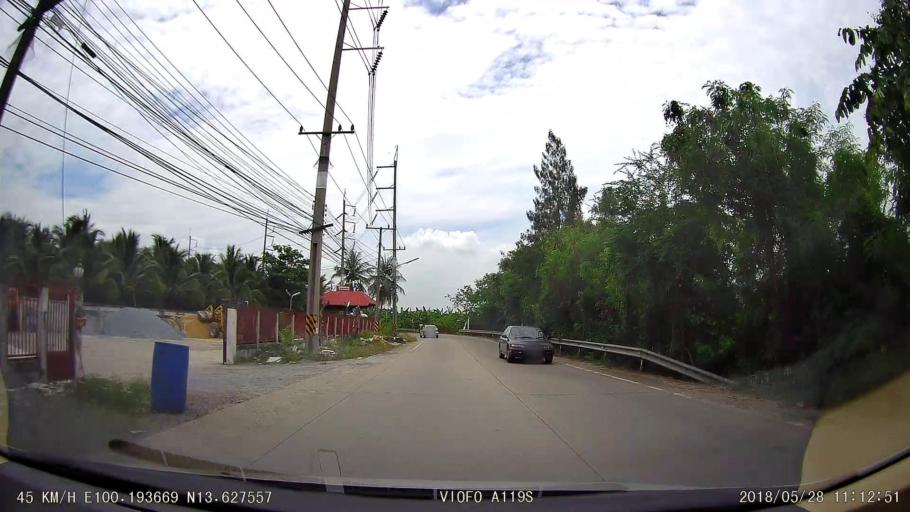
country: TH
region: Samut Sakhon
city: Krathum Baen
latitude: 13.6275
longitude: 100.1939
